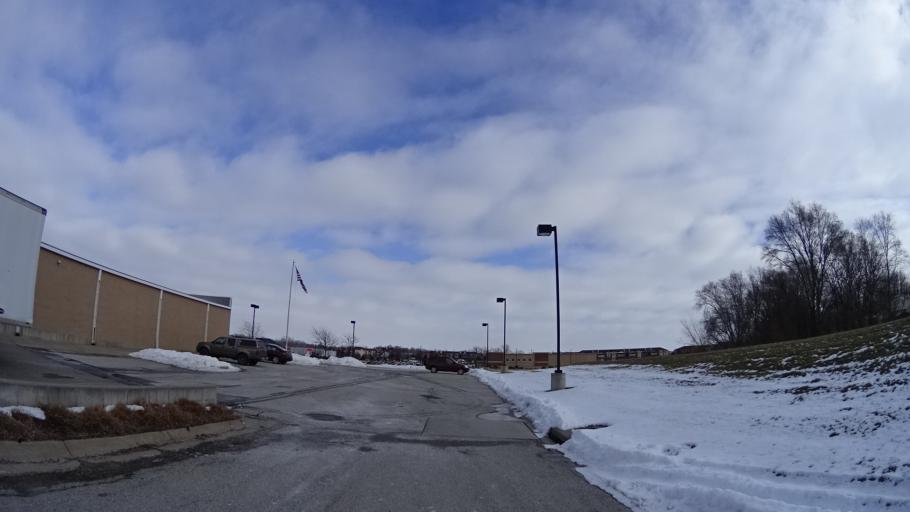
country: US
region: Nebraska
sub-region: Sarpy County
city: Offutt Air Force Base
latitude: 41.1166
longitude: -95.9455
